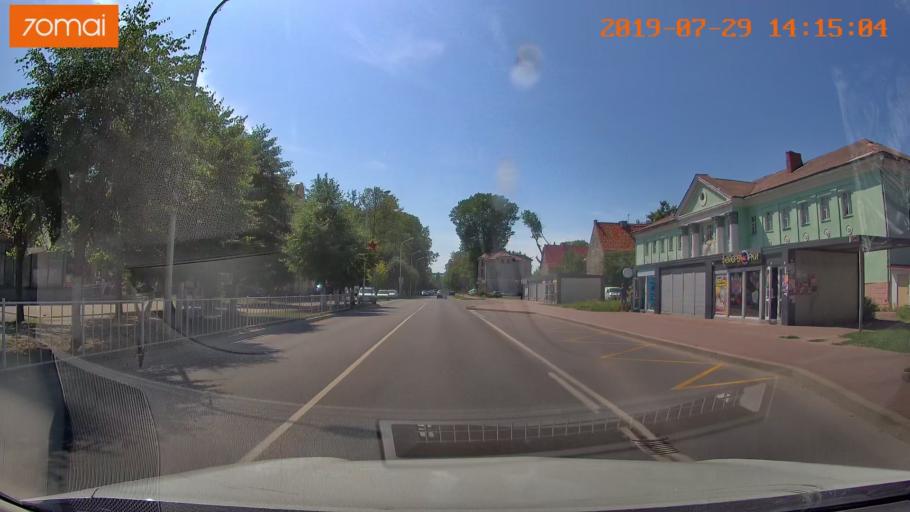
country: RU
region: Kaliningrad
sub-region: Gorod Kaliningrad
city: Baltiysk
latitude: 54.6484
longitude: 19.9021
